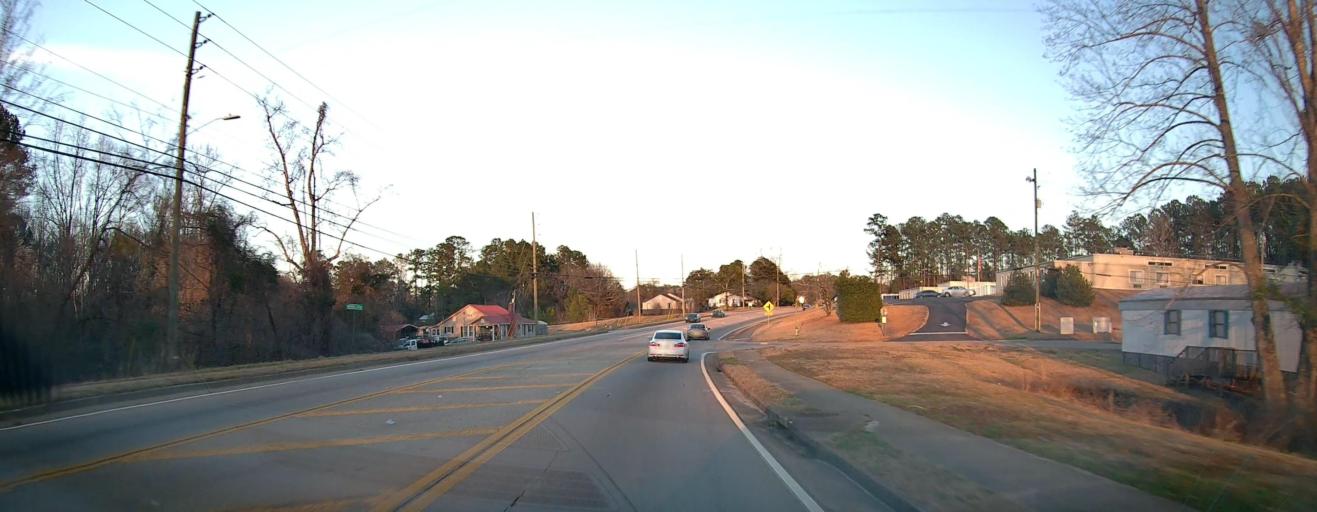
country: US
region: Georgia
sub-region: Troup County
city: La Grange
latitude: 33.0558
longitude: -84.9971
